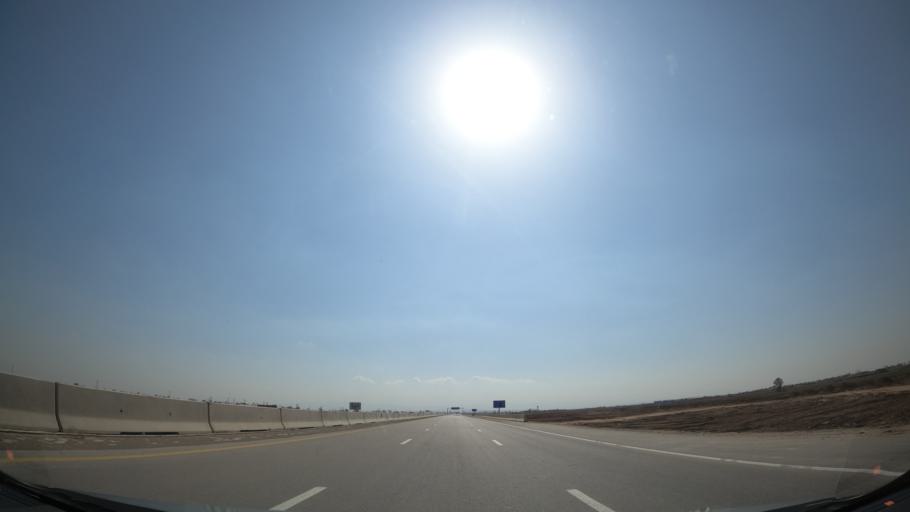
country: IR
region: Qazvin
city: Abyek
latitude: 35.9765
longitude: 50.4616
